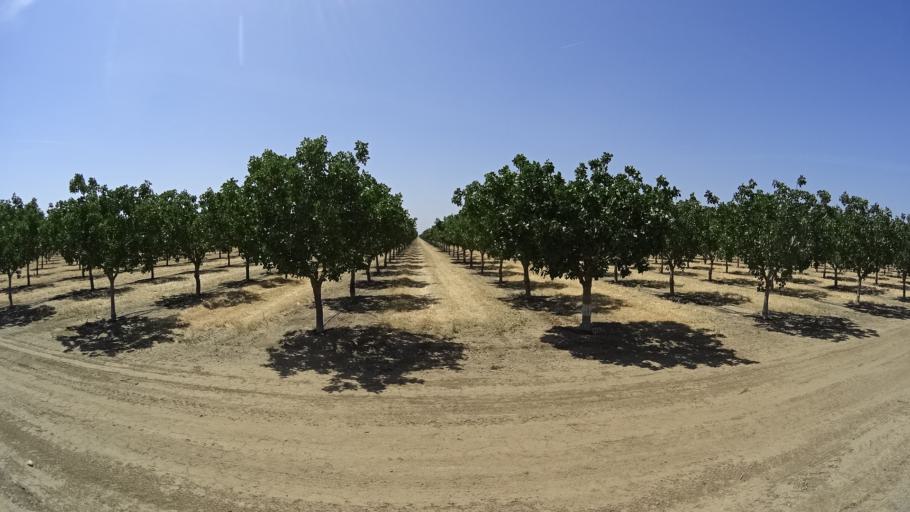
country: US
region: California
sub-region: Kings County
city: Kettleman City
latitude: 36.1377
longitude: -119.9617
